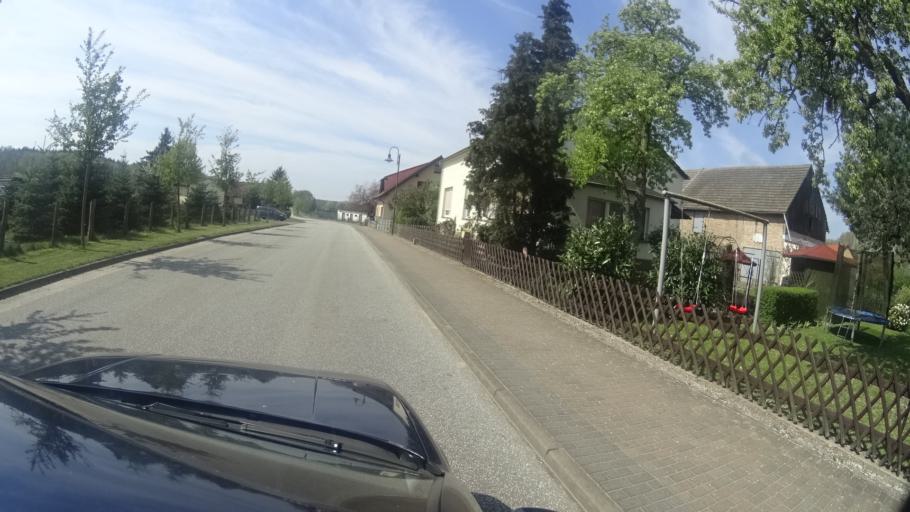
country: DE
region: Brandenburg
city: Dreetz
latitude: 52.7408
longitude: 12.4888
